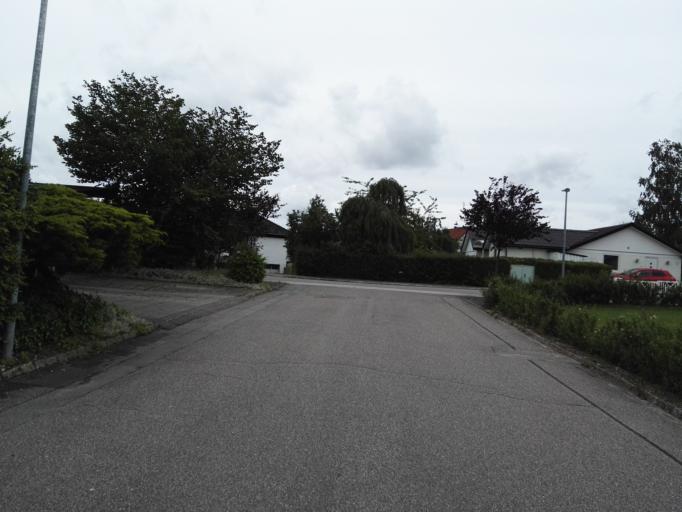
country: DK
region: Capital Region
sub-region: Egedal Kommune
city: Stenlose
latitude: 55.7701
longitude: 12.1879
